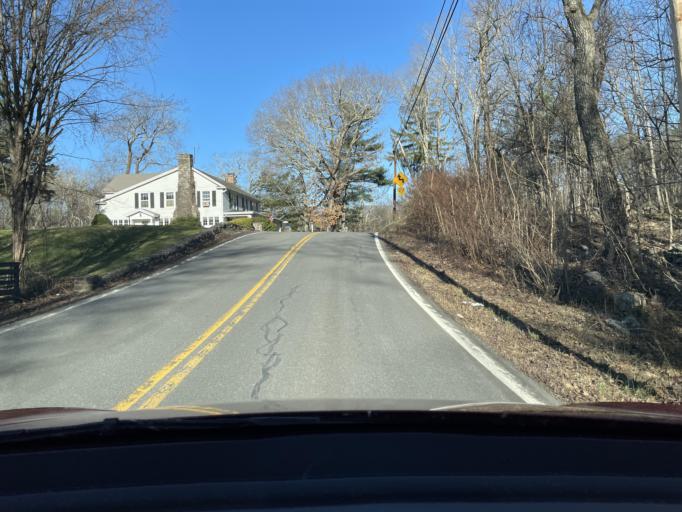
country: US
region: New York
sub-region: Ulster County
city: Zena
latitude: 42.0453
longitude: -74.0256
